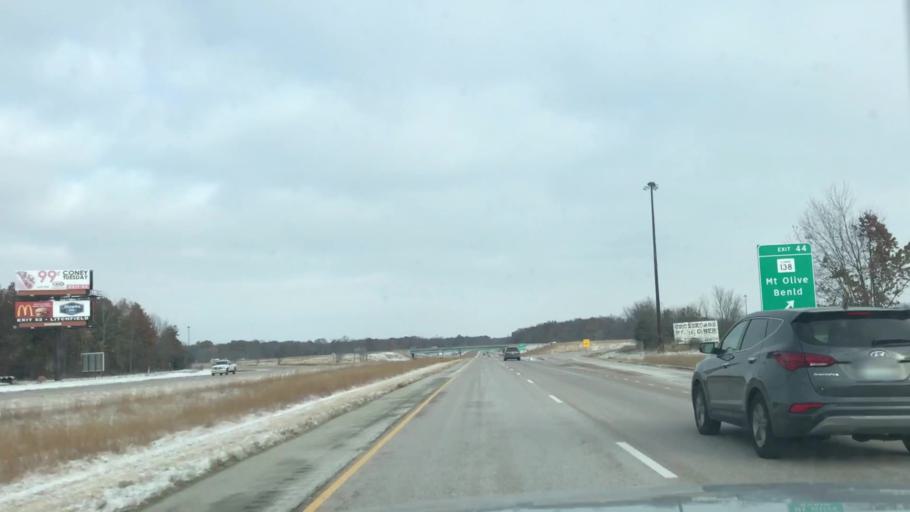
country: US
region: Illinois
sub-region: Macoupin County
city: Mount Olive
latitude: 39.0672
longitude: -89.7556
